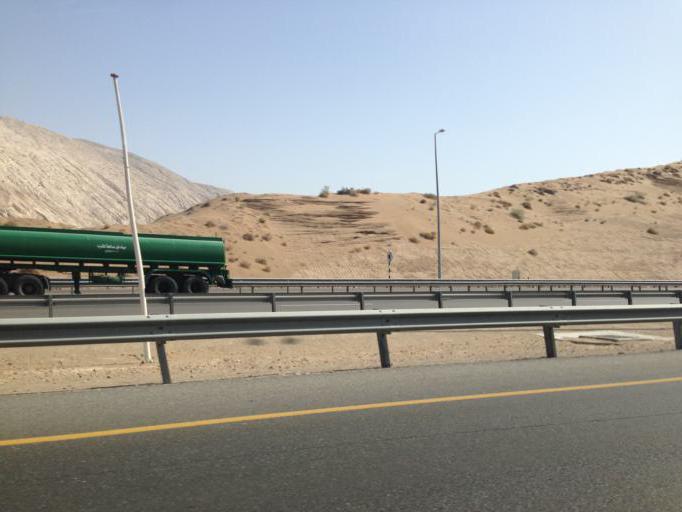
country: OM
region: Muhafazat Masqat
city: Bawshar
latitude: 23.5712
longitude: 58.4215
